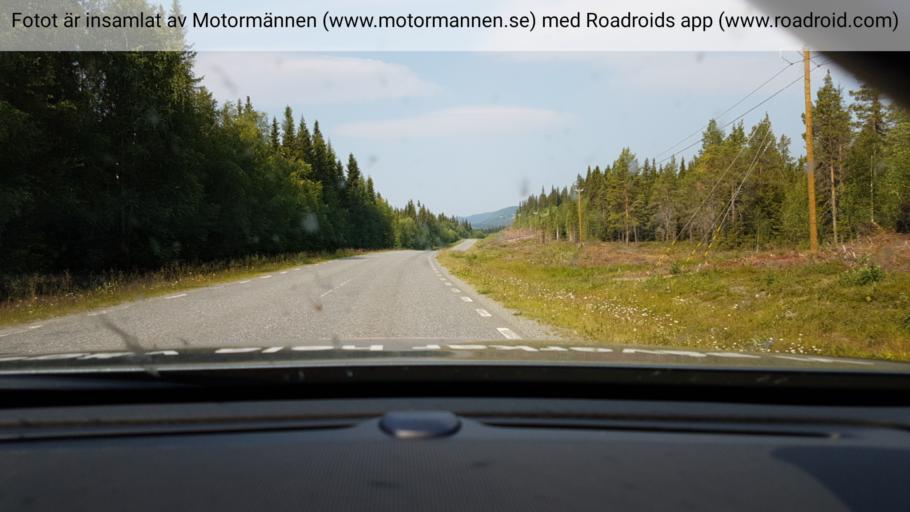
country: SE
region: Vaesterbotten
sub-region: Vilhelmina Kommun
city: Sjoberg
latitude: 65.4752
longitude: 16.0183
